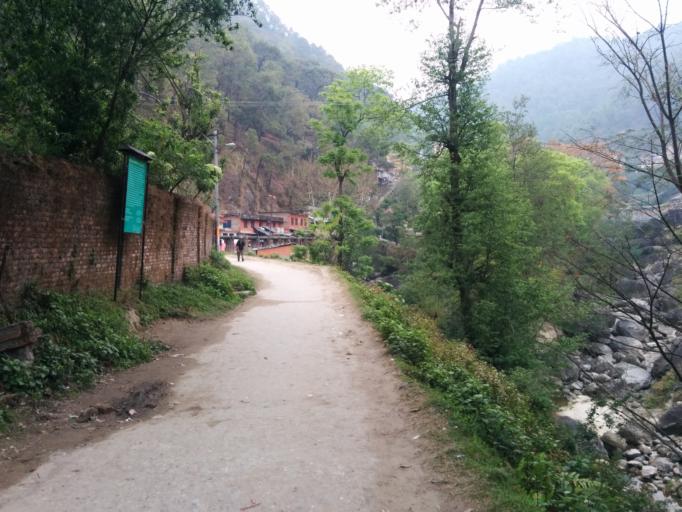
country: NP
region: Central Region
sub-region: Bagmati Zone
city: Bhaktapur
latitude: 27.7603
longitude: 85.4211
